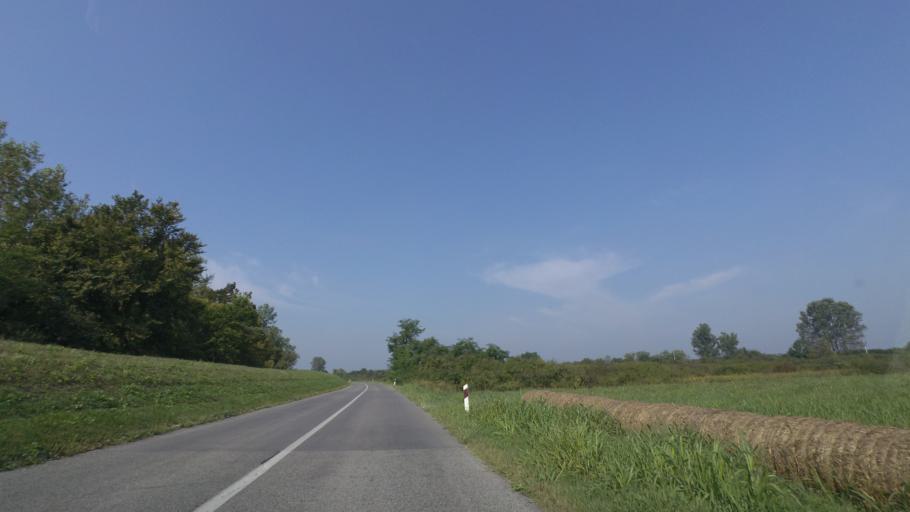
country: BA
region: Republika Srpska
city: Bosanska Dubica
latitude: 45.2348
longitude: 16.8458
